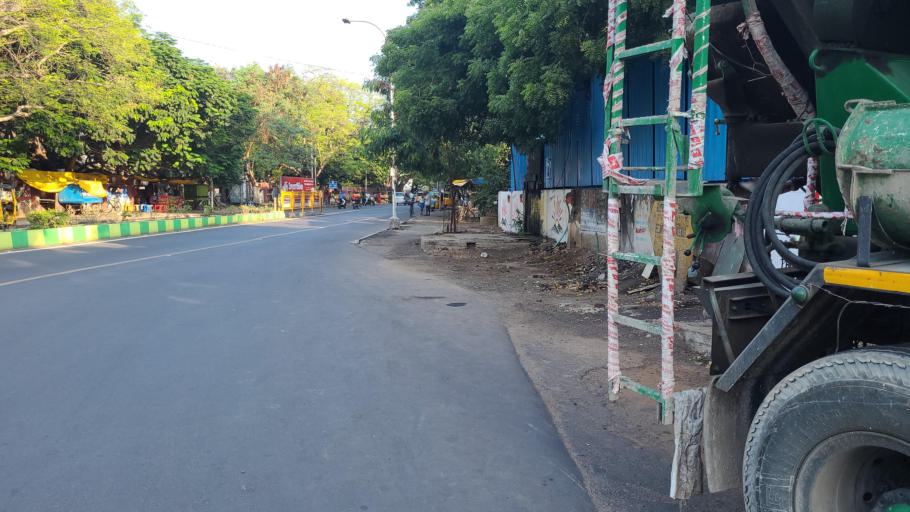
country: IN
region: Tamil Nadu
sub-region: Chennai
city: Gandhi Nagar
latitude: 13.0000
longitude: 80.2667
